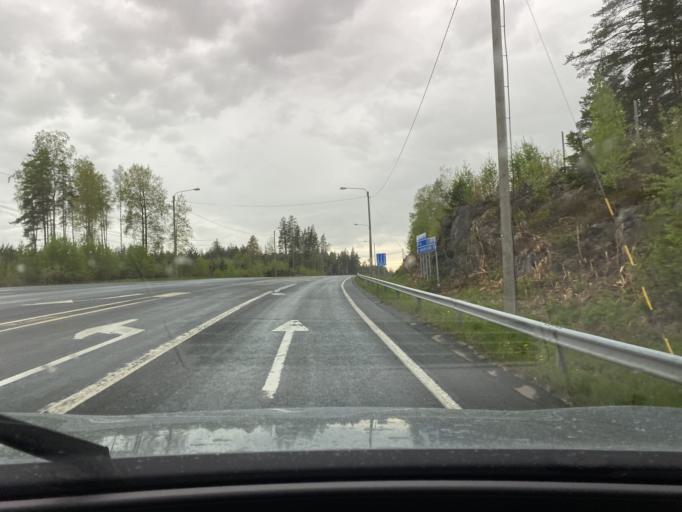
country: FI
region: Varsinais-Suomi
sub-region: Salo
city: Suomusjaervi
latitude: 60.3711
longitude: 23.6441
